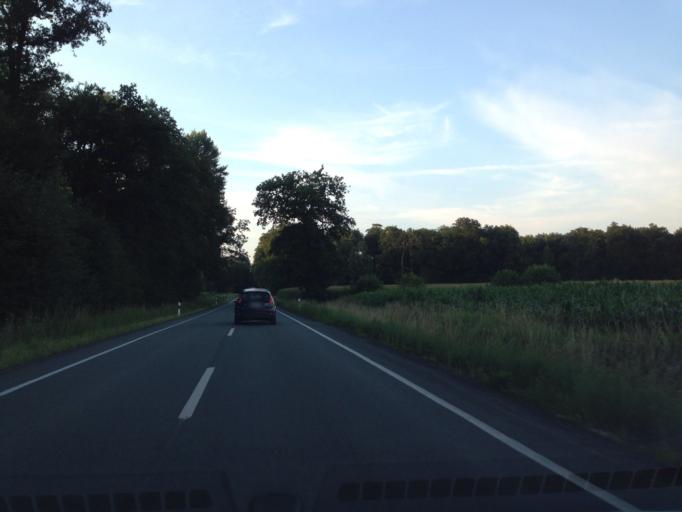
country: DE
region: North Rhine-Westphalia
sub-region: Regierungsbezirk Munster
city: Senden
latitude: 51.8354
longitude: 7.5422
